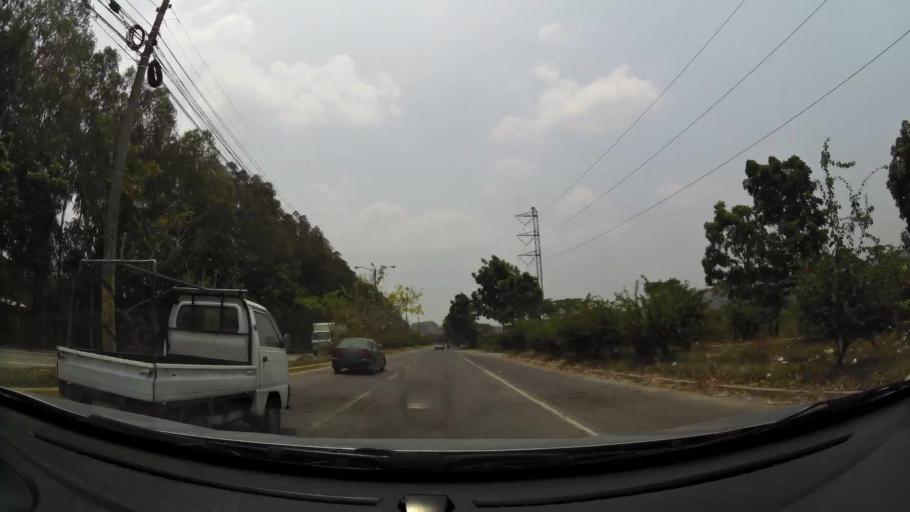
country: HN
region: Cortes
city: Chotepe
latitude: 15.4696
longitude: -87.9672
